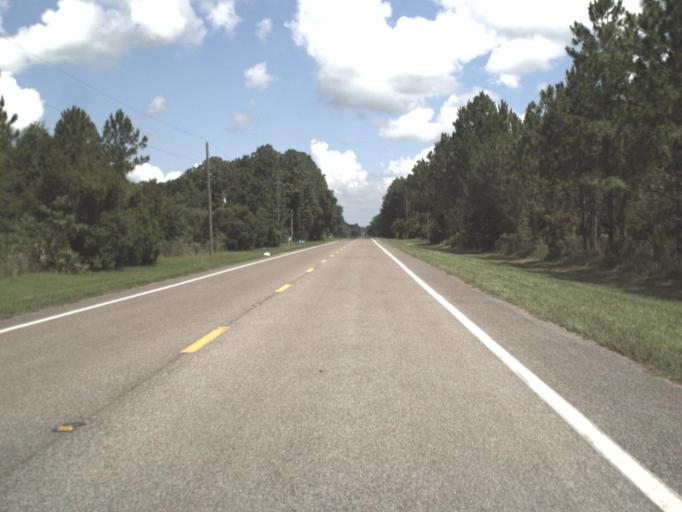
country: US
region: Florida
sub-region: Putnam County
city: East Palatka
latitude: 29.5631
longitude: -81.5430
